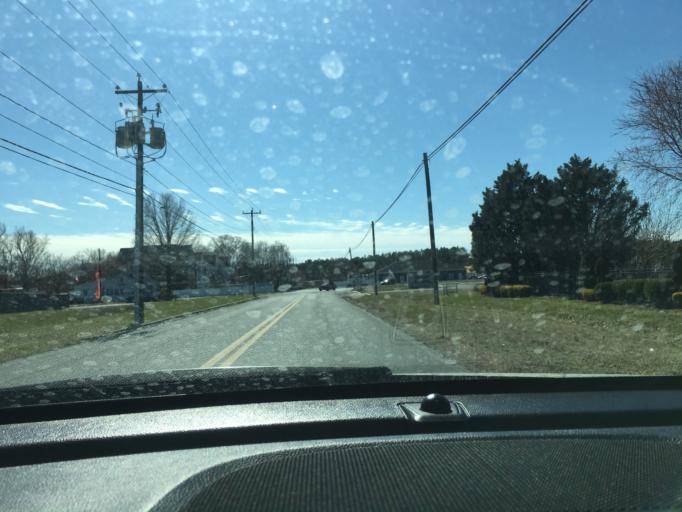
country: US
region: Maryland
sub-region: Wicomico County
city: Salisbury
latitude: 38.4034
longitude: -75.5715
